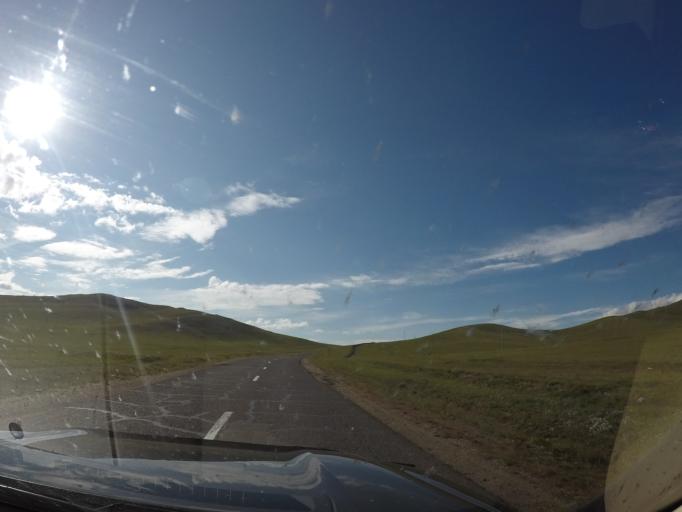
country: MN
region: Hentiy
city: Modot
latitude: 47.7723
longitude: 108.8611
